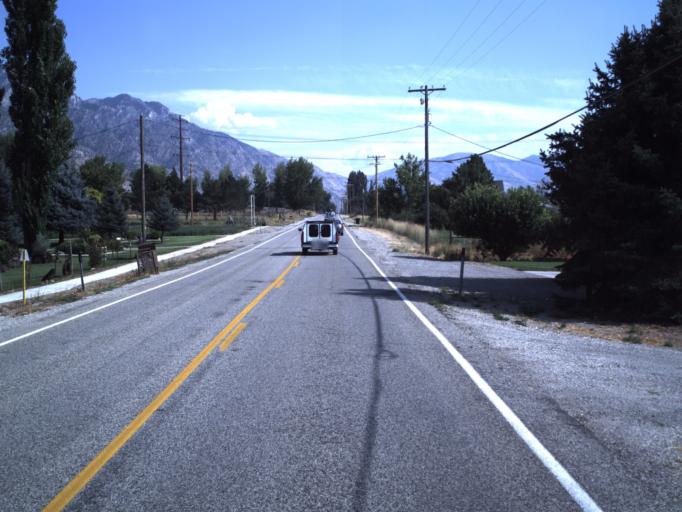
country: US
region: Utah
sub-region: Box Elder County
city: Honeyville
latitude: 41.6117
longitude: -112.0632
